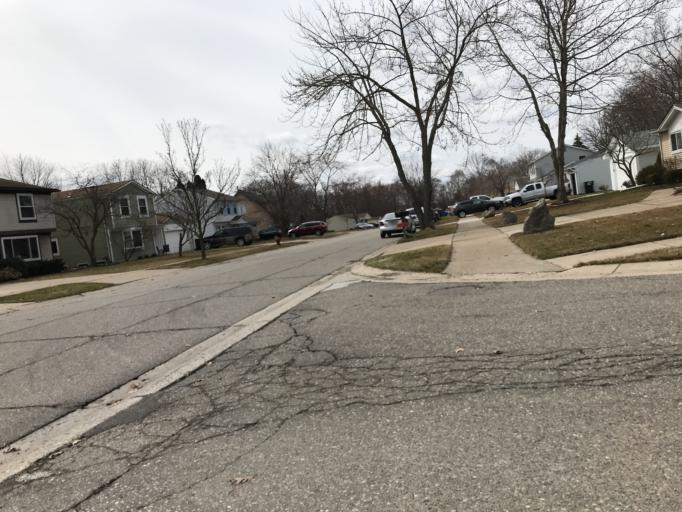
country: US
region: Michigan
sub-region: Oakland County
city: South Lyon
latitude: 42.4678
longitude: -83.6398
